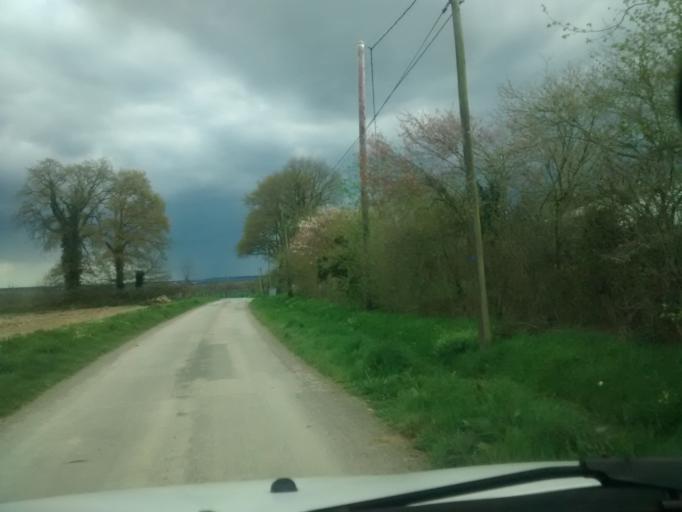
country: FR
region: Brittany
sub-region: Departement d'Ille-et-Vilaine
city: Servon-sur-Vilaine
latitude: 48.1527
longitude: -1.4911
